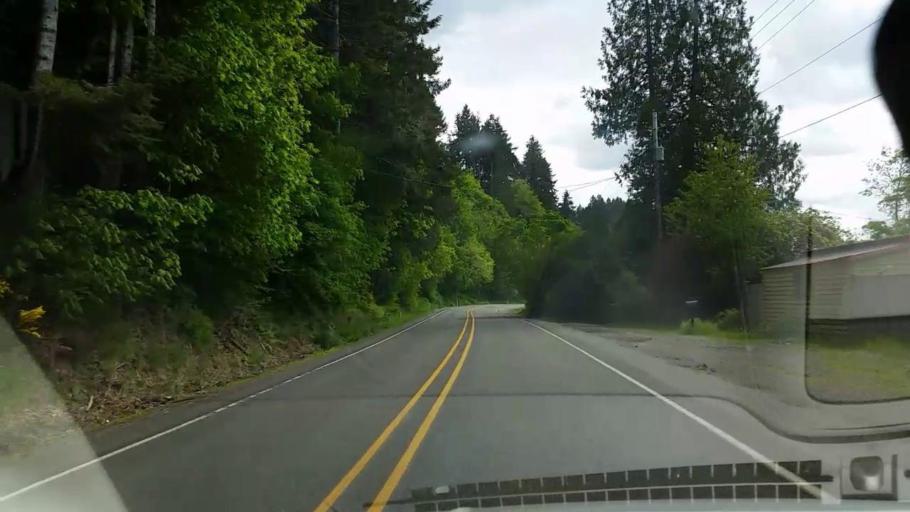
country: US
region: Washington
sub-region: Mason County
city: Shelton
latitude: 47.3409
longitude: -123.1099
